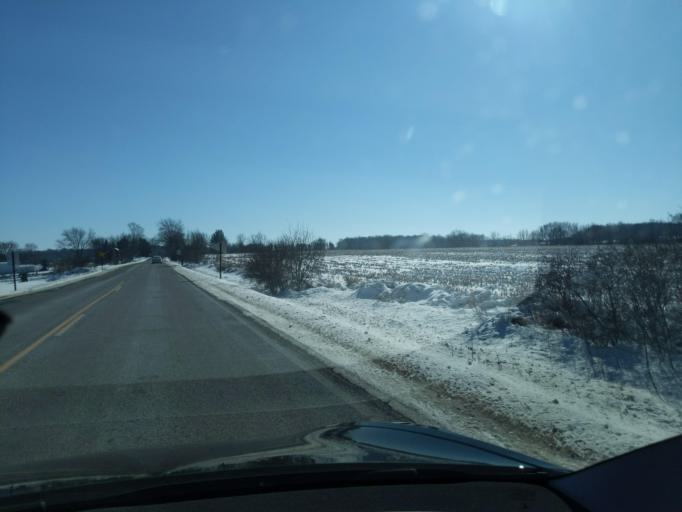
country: US
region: Michigan
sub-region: Livingston County
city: Fowlerville
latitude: 42.5509
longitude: -84.0707
